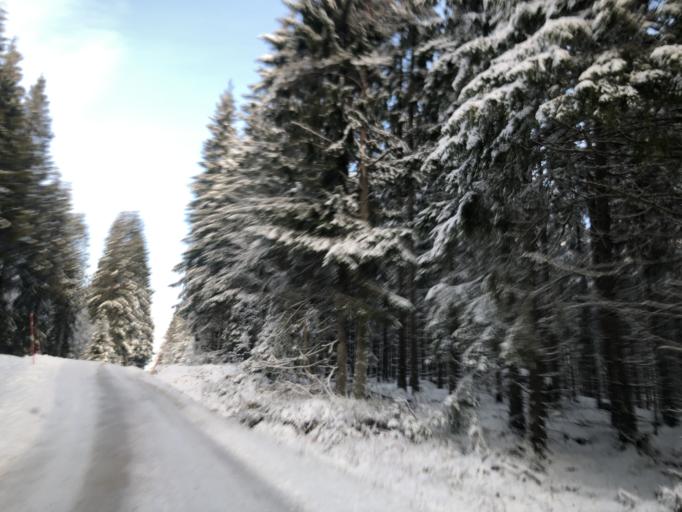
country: SE
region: Vaestra Goetaland
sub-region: Ulricehamns Kommun
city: Ulricehamn
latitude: 57.7499
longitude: 13.5086
